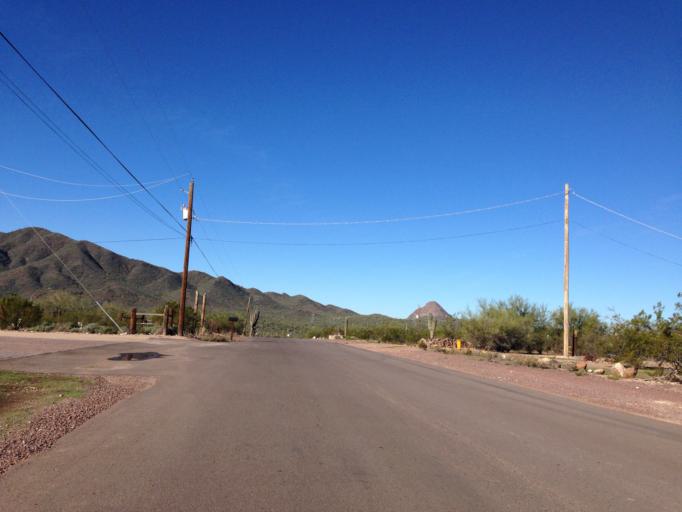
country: US
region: Arizona
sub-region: Maricopa County
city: New River
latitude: 33.8953
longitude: -112.0724
